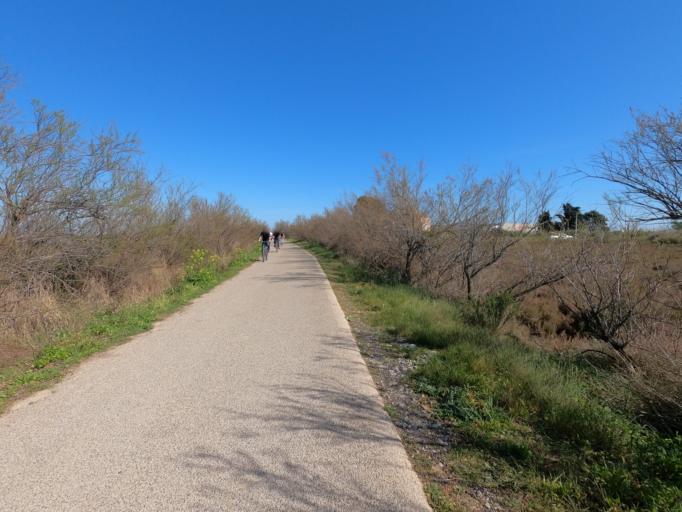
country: FR
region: Languedoc-Roussillon
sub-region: Departement de l'Herault
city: Palavas-les-Flots
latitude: 43.5362
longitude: 3.9069
